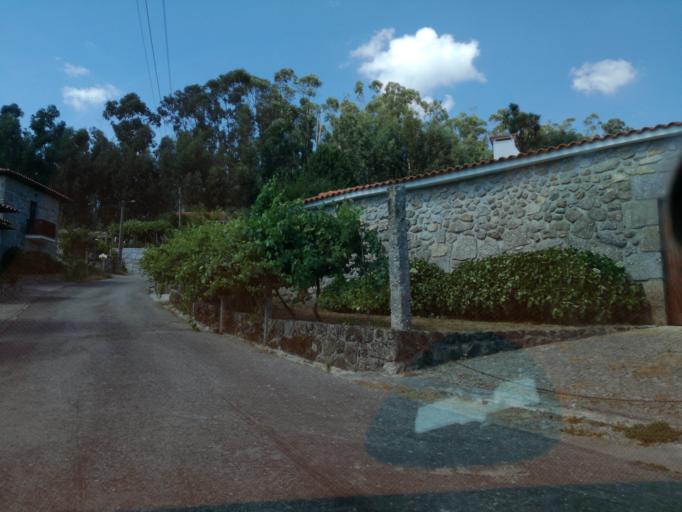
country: PT
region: Braga
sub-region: Fafe
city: Aroes
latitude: 41.4945
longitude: -8.2301
